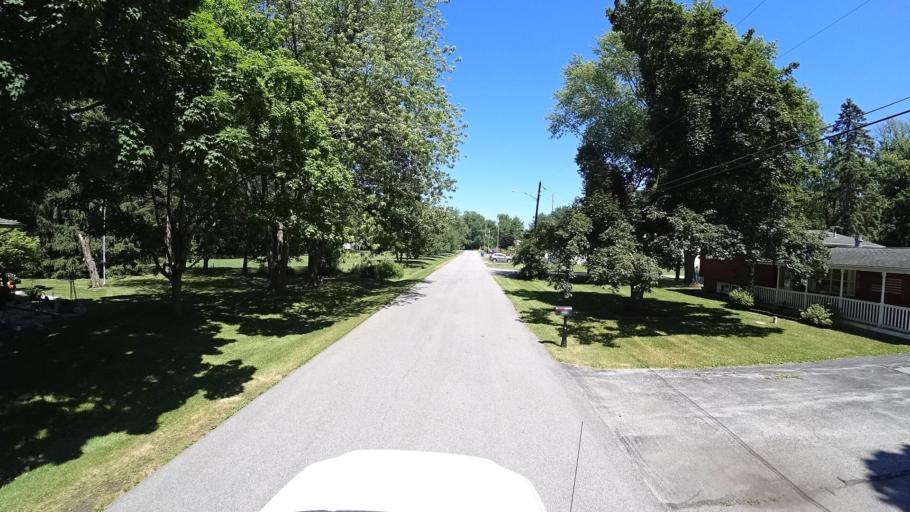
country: US
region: Indiana
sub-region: Porter County
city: Porter
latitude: 41.6020
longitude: -87.0841
